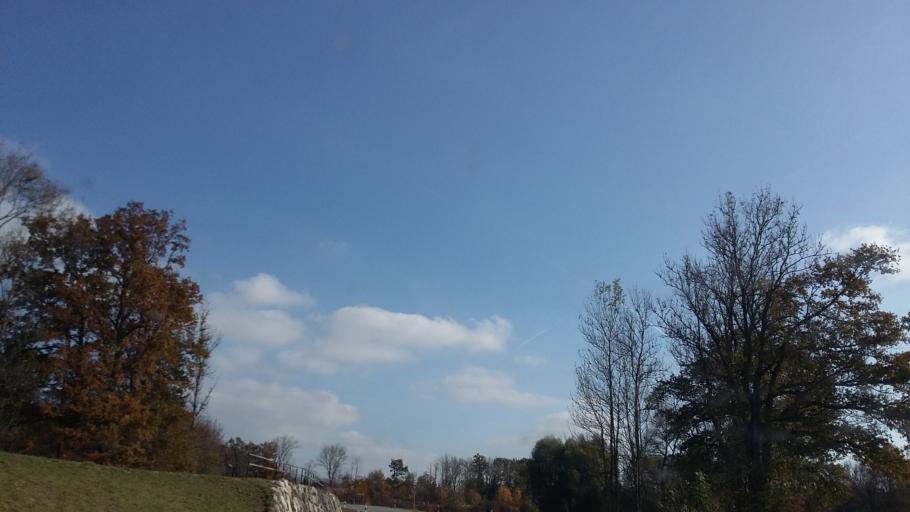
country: DE
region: Bavaria
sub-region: Upper Bavaria
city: Bad Aibling
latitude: 47.8596
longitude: 11.9837
